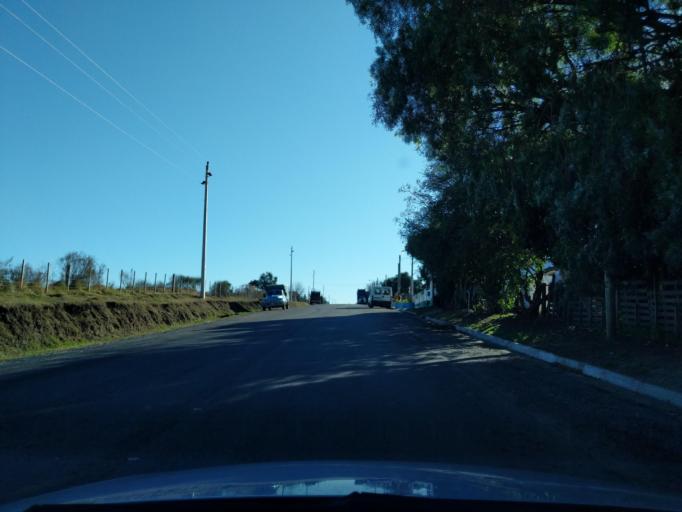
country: UY
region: Florida
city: Florida
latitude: -34.1008
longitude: -56.2417
